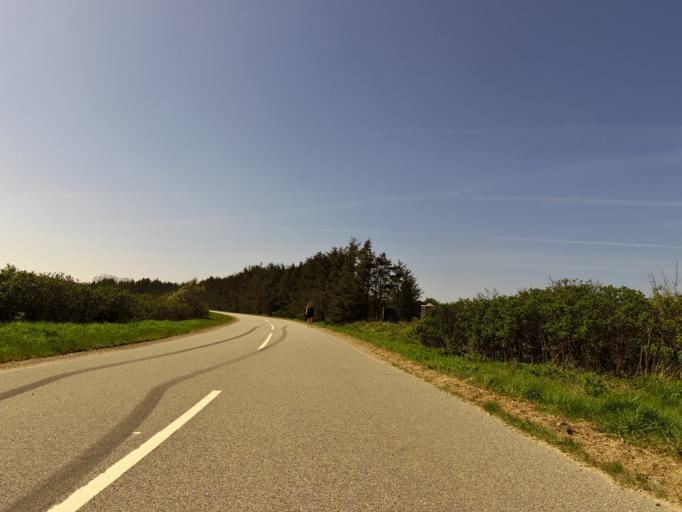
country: DK
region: Central Jutland
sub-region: Struer Kommune
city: Struer
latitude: 56.5189
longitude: 8.6077
